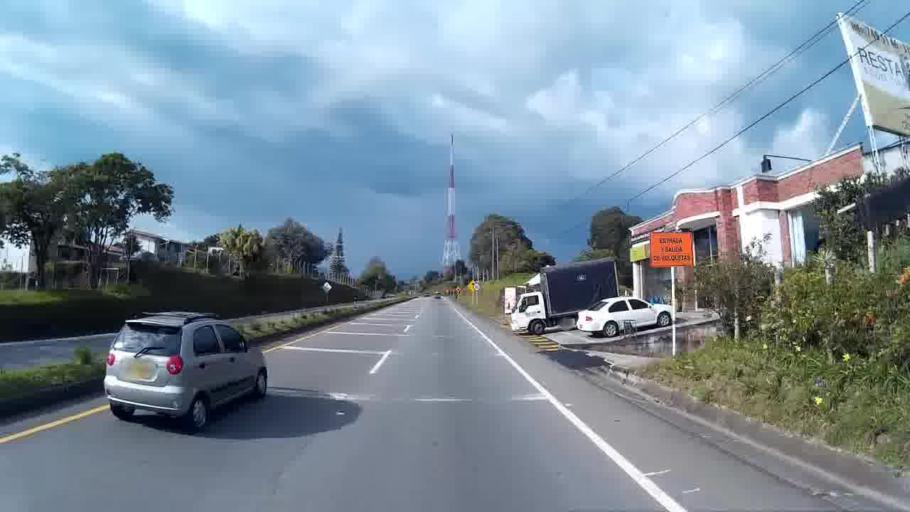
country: CO
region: Quindio
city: Circasia
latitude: 4.6095
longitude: -75.6321
